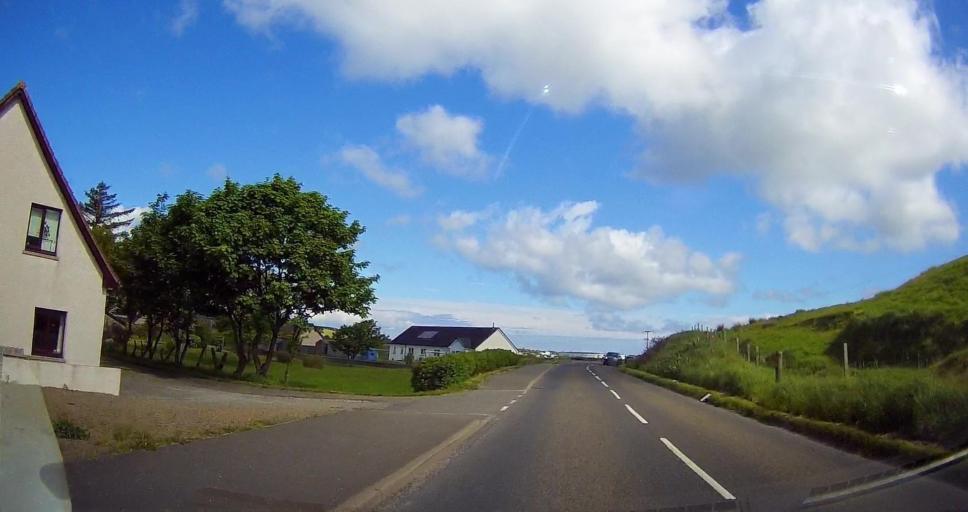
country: GB
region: Scotland
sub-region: Orkney Islands
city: Orkney
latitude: 58.9610
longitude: -2.9686
